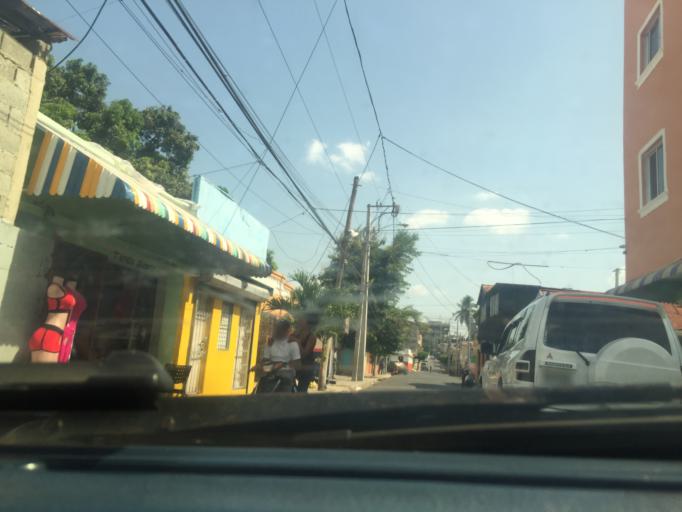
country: DO
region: Santiago
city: Santiago de los Caballeros
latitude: 19.4603
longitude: -70.7051
